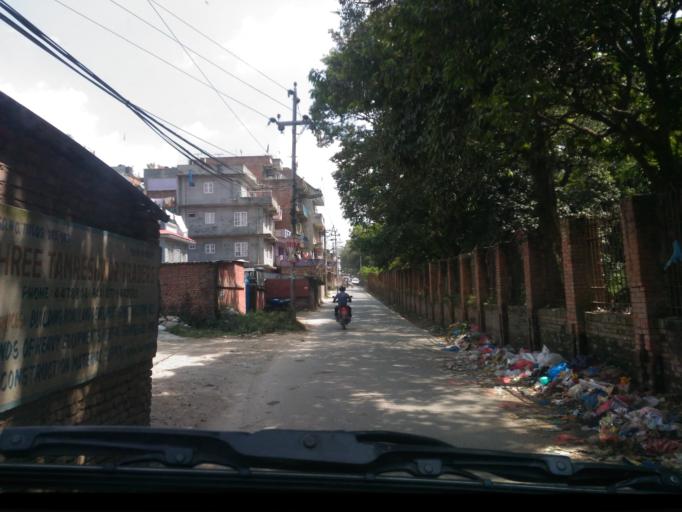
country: NP
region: Central Region
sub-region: Bagmati Zone
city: Kathmandu
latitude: 27.7112
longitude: 85.3417
